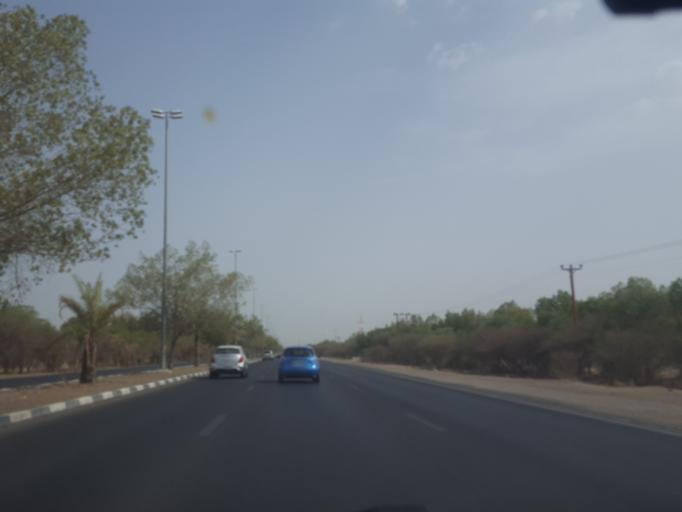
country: AE
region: Abu Dhabi
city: Al Ain
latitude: 24.1797
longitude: 55.7952
